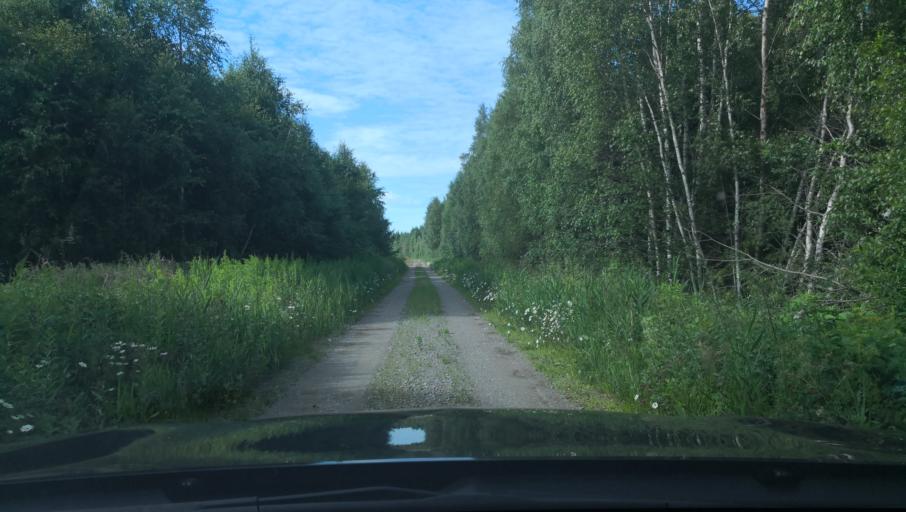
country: SE
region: Vaestmanland
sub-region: Surahammars Kommun
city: Surahammar
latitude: 59.6650
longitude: 16.1055
